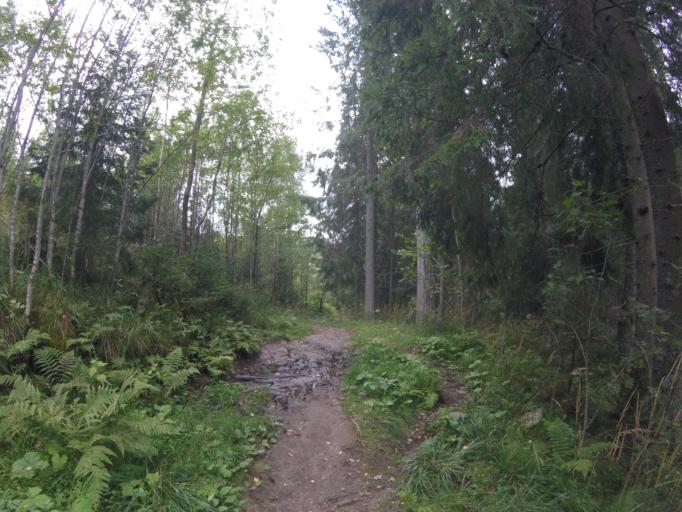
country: NO
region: Akershus
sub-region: Raelingen
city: Fjerdingby
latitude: 59.9124
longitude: 11.0351
